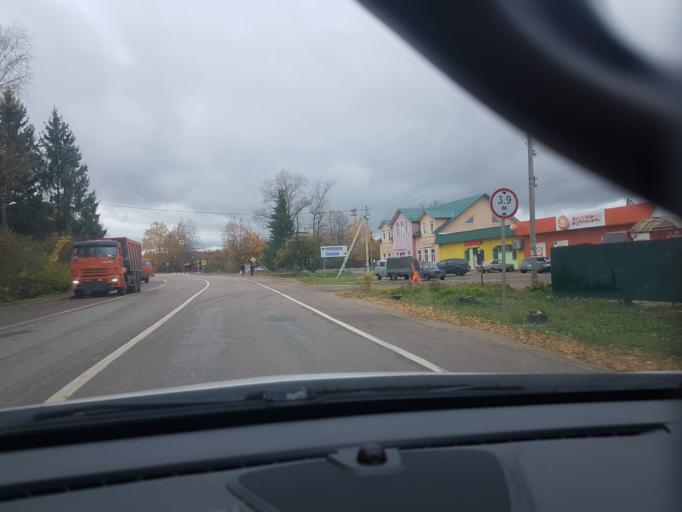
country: RU
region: Moskovskaya
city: Novopetrovskoye
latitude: 56.0084
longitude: 36.3462
